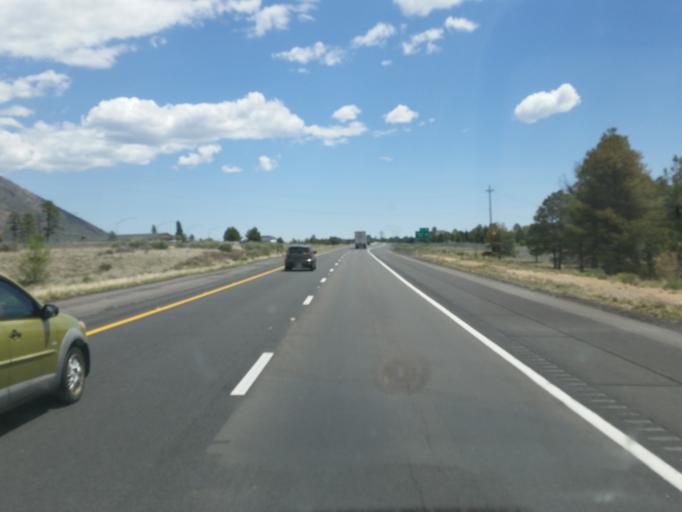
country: US
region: Arizona
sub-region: Coconino County
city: Flagstaff
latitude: 35.1876
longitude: -111.6282
